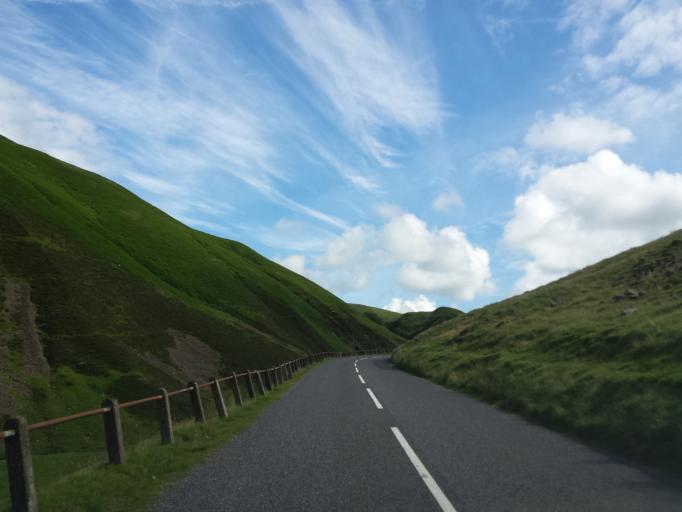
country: GB
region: Scotland
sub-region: Dumfries and Galloway
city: Moffat
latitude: 55.4228
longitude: -3.2769
